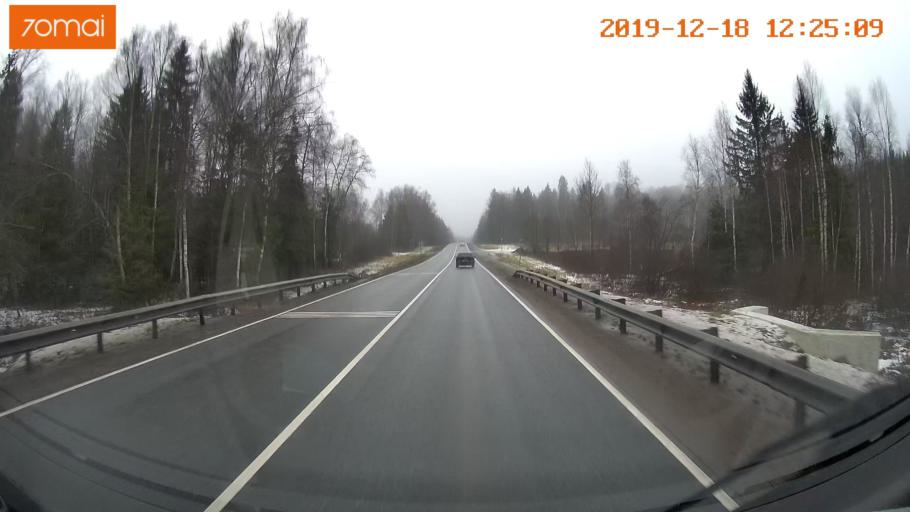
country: RU
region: Moskovskaya
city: Novopetrovskoye
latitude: 56.0340
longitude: 36.5000
